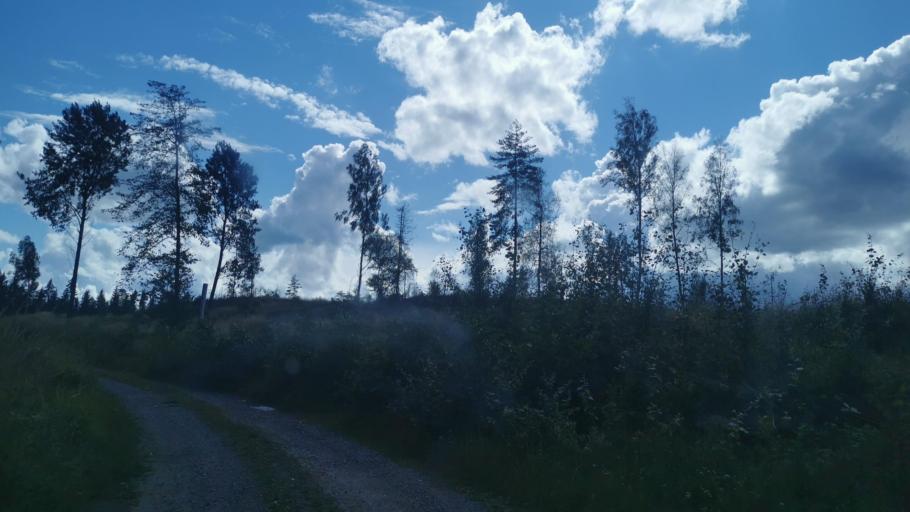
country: SE
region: OEstergoetland
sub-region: Finspangs Kommun
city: Finspang
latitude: 58.7985
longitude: 15.8044
